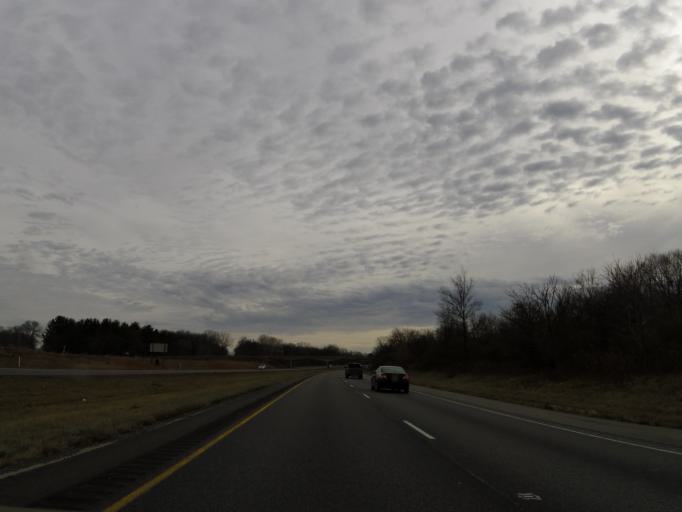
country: US
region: Indiana
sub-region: Hendricks County
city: Pittsboro
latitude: 39.8797
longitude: -86.4432
